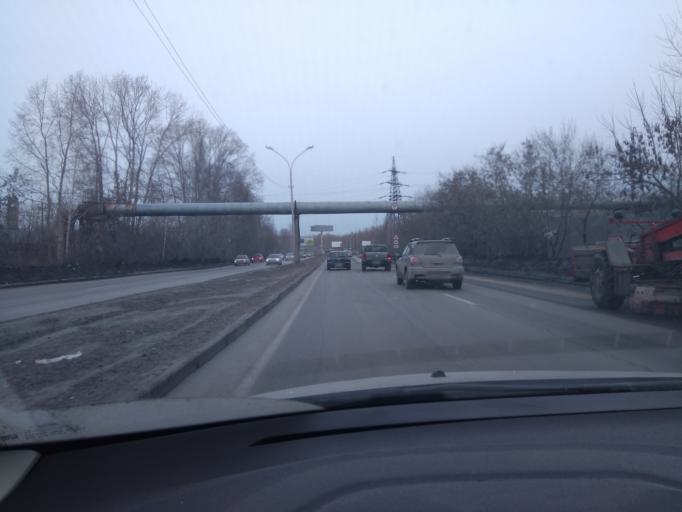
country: RU
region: Sverdlovsk
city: Yekaterinburg
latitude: 56.8512
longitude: 60.6712
